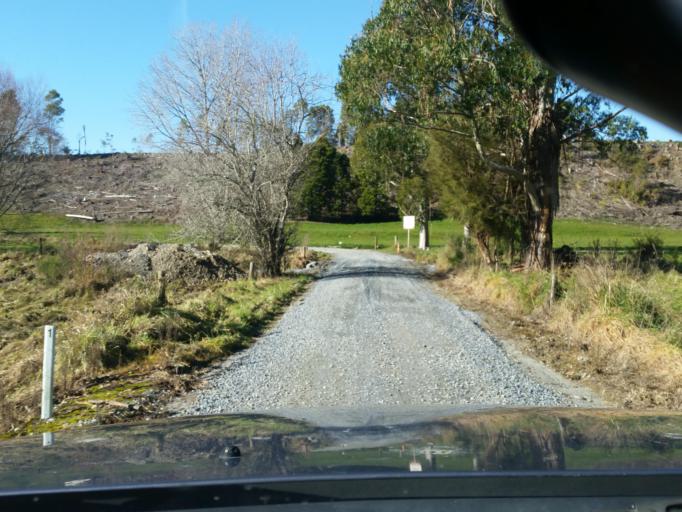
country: NZ
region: Tasman
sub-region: Tasman District
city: Takaka
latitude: -40.8419
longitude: 172.7774
